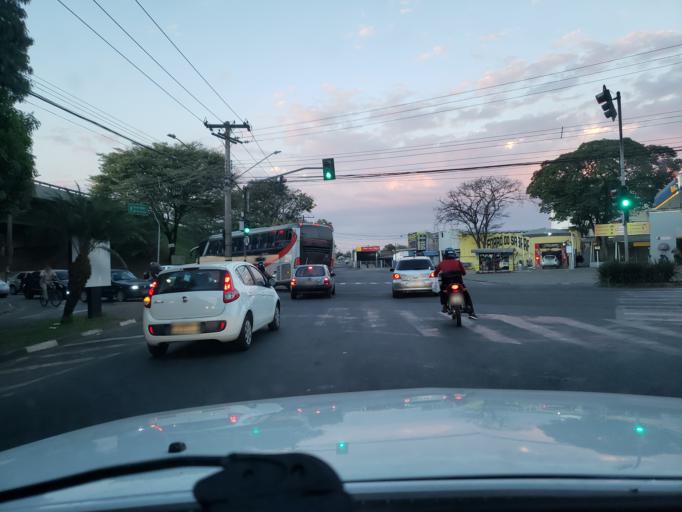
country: BR
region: Sao Paulo
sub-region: Moji-Guacu
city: Mogi-Gaucu
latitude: -22.3443
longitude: -46.9480
